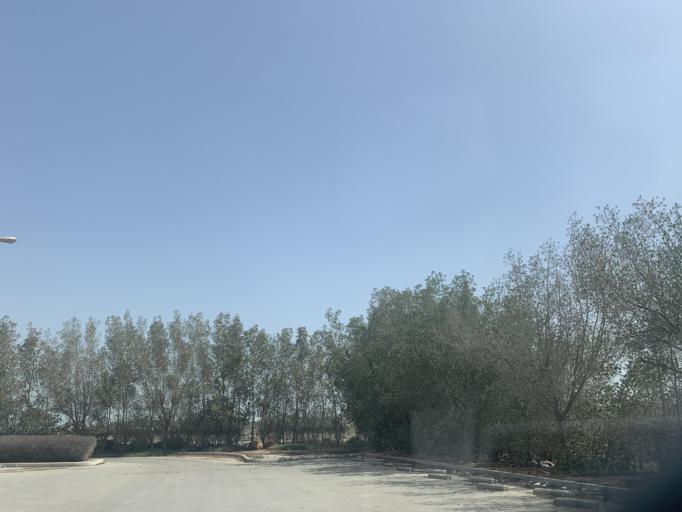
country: BH
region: Manama
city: Jidd Hafs
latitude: 26.2001
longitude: 50.5467
